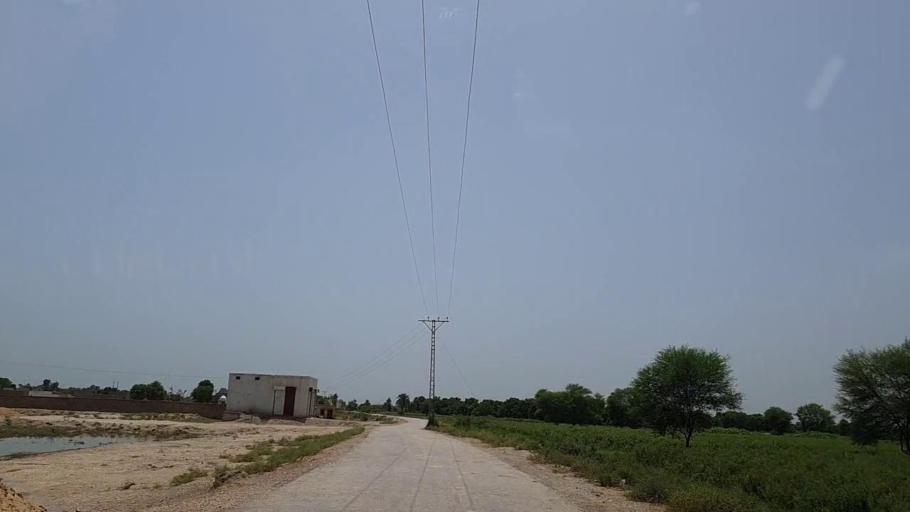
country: PK
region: Sindh
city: Tharu Shah
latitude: 26.9451
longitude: 68.1068
